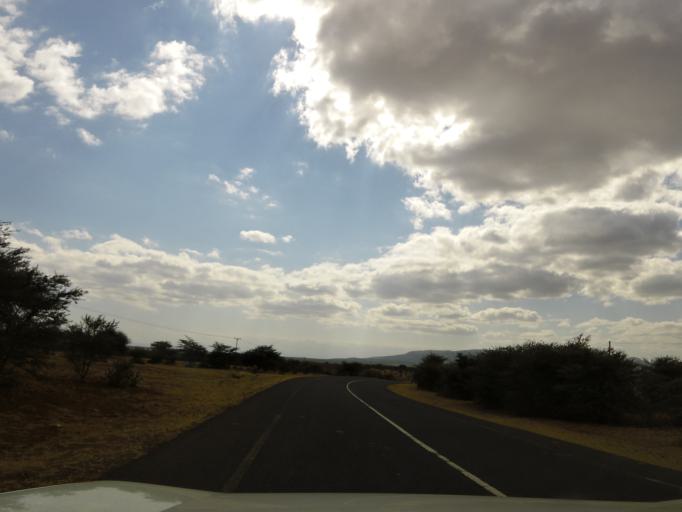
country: TZ
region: Arusha
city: Mto wa Mbu
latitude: -3.5354
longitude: 36.0773
